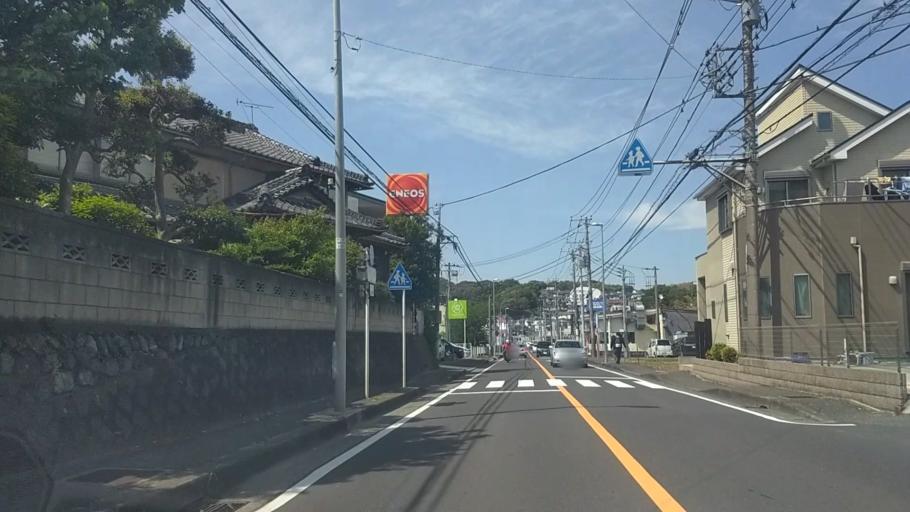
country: JP
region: Kanagawa
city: Kamakura
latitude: 35.3537
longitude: 139.5798
